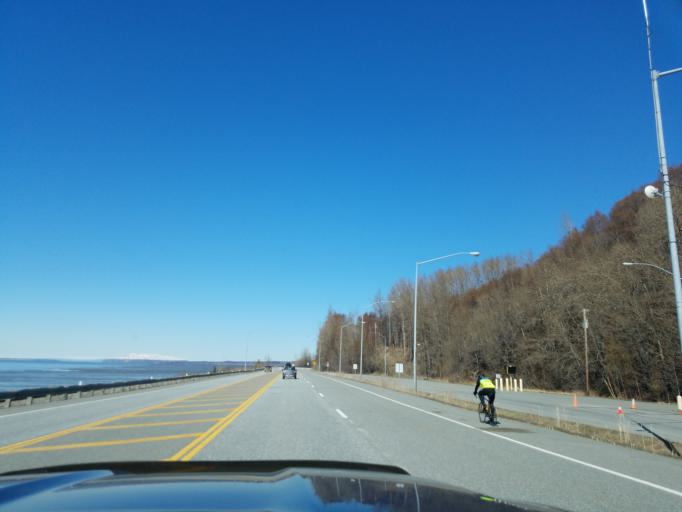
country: US
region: Alaska
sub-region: Anchorage Municipality
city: Anchorage
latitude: 61.0452
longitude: -149.7896
